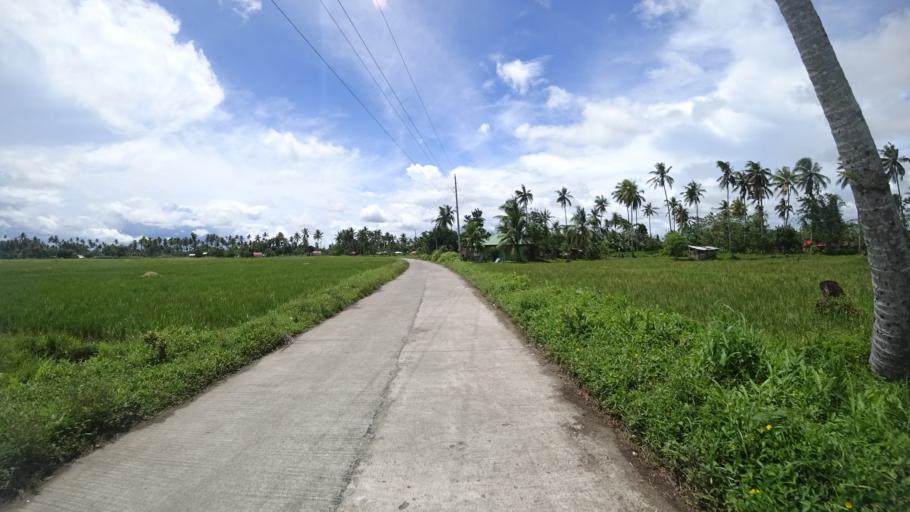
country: PH
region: Eastern Visayas
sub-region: Province of Leyte
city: Alangalang
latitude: 11.2283
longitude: 124.8458
